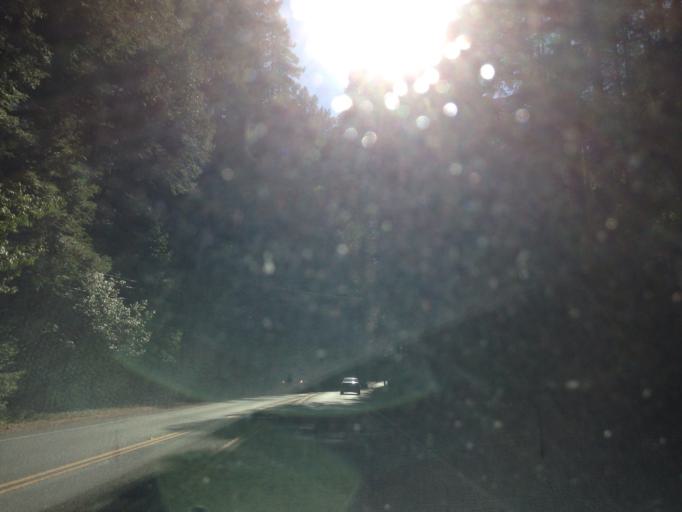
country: US
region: California
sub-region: Sonoma County
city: Monte Rio
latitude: 38.4771
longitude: -122.9994
